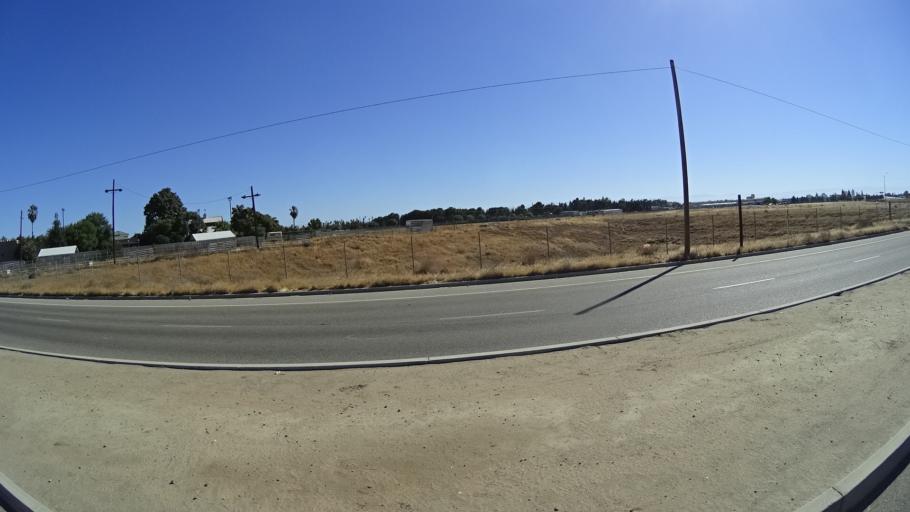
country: US
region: California
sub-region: Fresno County
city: West Park
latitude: 36.7400
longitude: -119.8345
